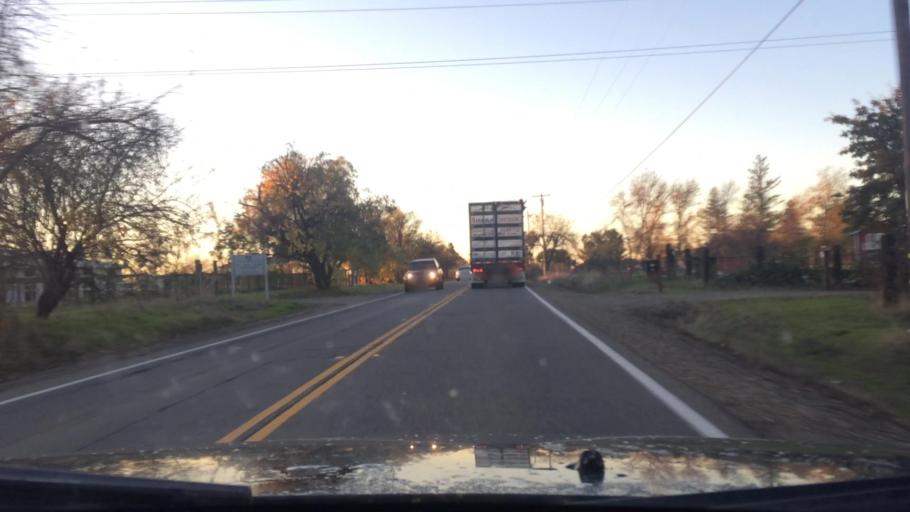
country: US
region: California
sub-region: Sacramento County
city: Vineyard
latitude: 38.5151
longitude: -121.2980
